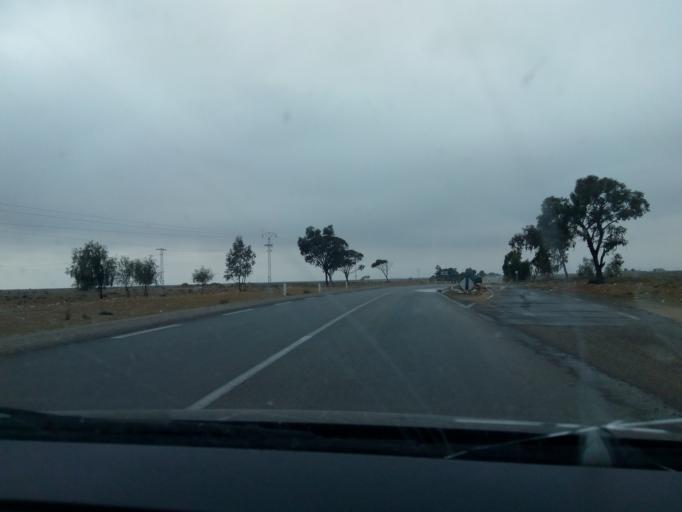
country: TN
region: Madanin
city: Medenine
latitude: 33.2723
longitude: 10.4682
